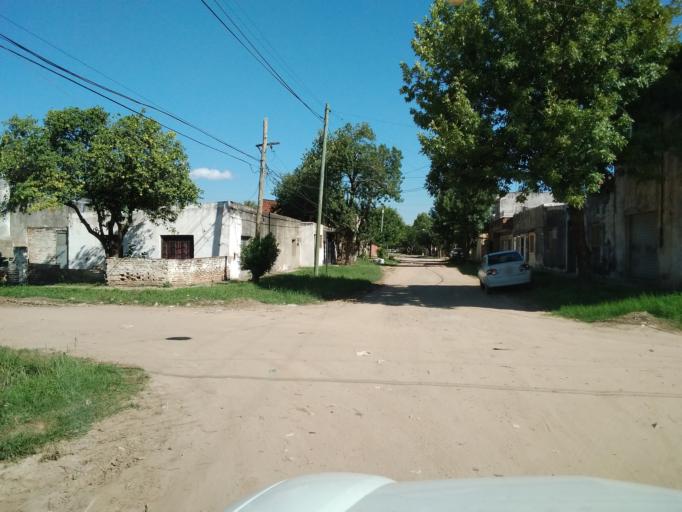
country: AR
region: Corrientes
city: Corrientes
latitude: -27.4800
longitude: -58.8089
